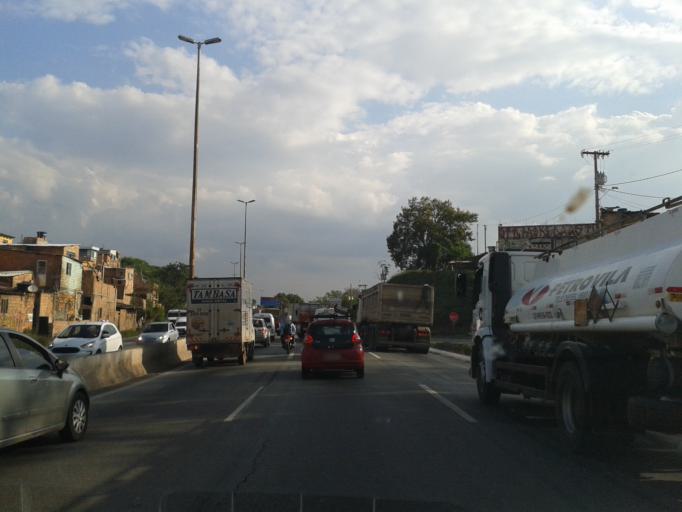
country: BR
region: Minas Gerais
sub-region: Belo Horizonte
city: Belo Horizonte
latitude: -19.8732
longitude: -43.9492
